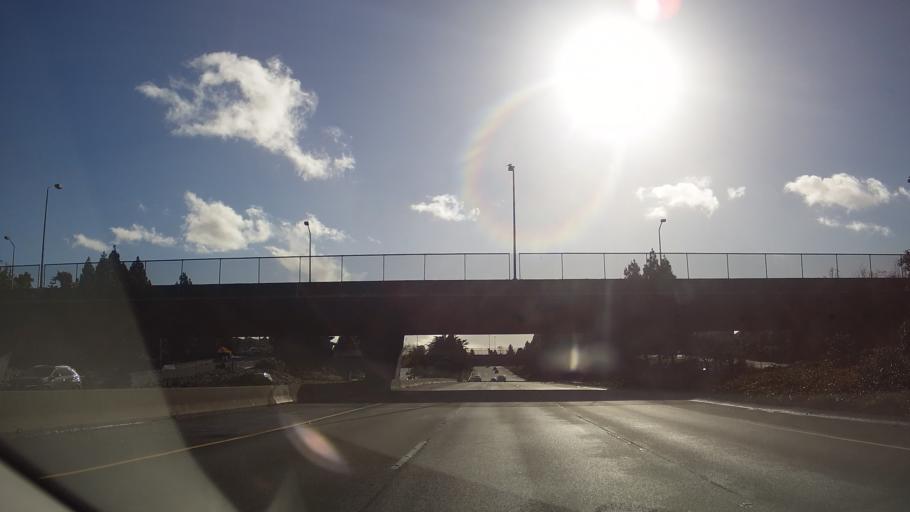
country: US
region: California
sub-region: Alameda County
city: Oakland
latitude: 37.8075
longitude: -122.2777
